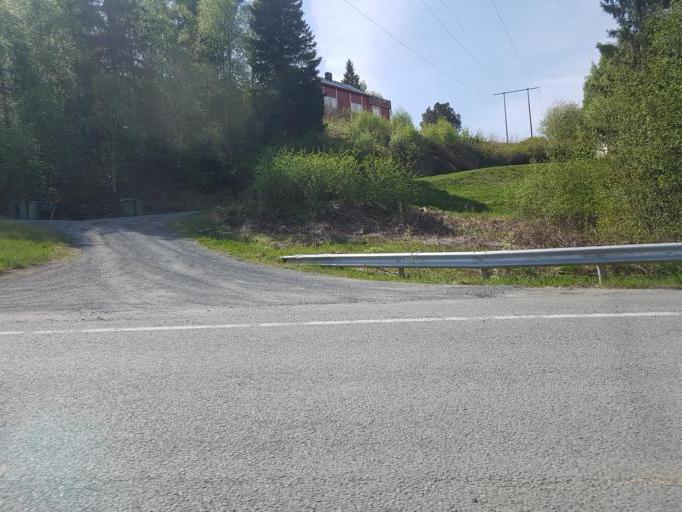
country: NO
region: Nord-Trondelag
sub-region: Levanger
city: Levanger
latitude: 63.7307
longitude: 11.2913
